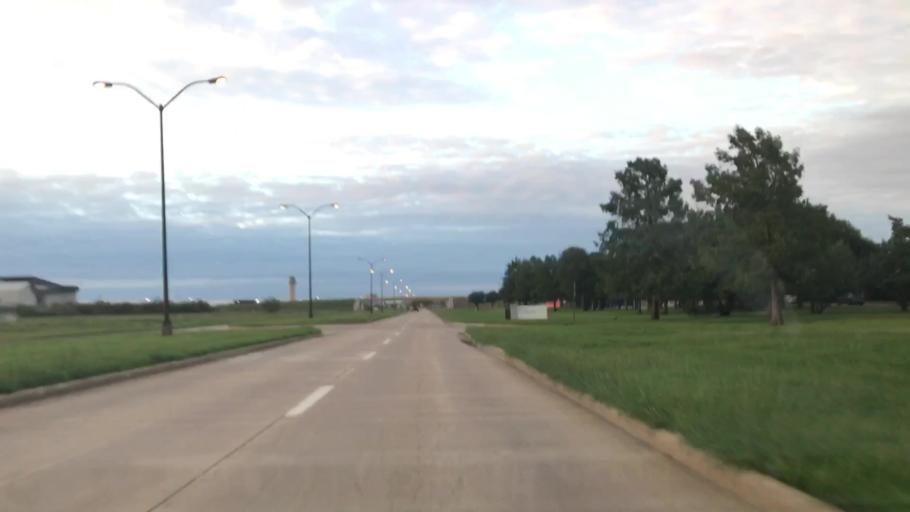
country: US
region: Texas
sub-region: Dallas County
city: Coppell
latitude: 32.8791
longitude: -97.0156
